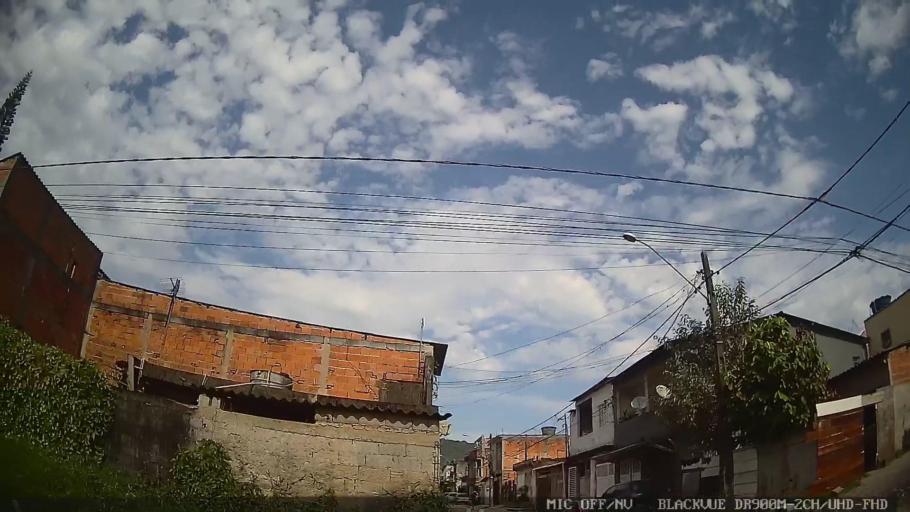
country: BR
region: Sao Paulo
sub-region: Guaruja
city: Guaruja
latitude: -23.9584
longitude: -46.2457
